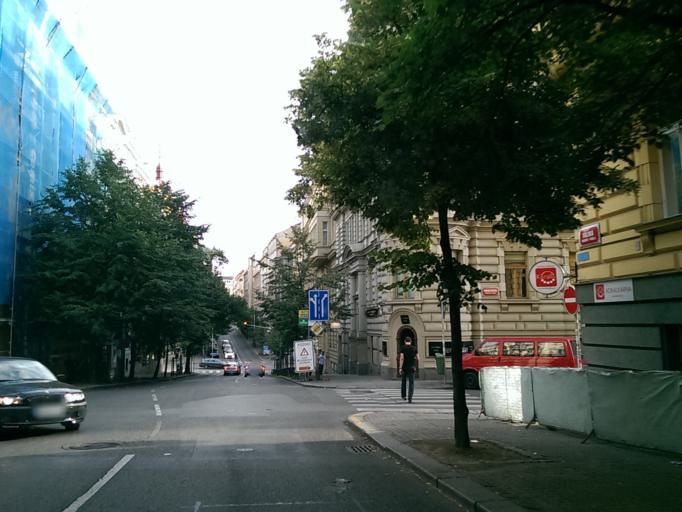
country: CZ
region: Praha
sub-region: Praha 8
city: Karlin
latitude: 50.0790
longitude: 14.4370
